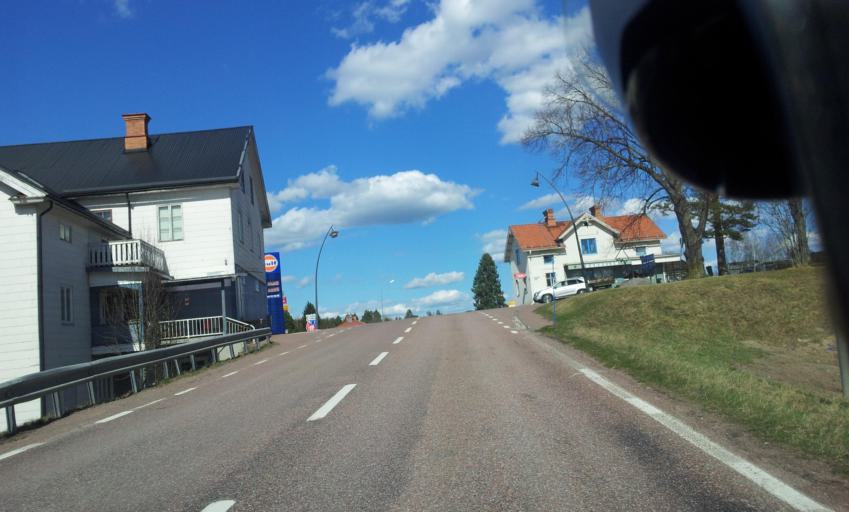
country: SE
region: Dalarna
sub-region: Faluns Kommun
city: Svardsjo
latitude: 60.8074
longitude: 15.7575
